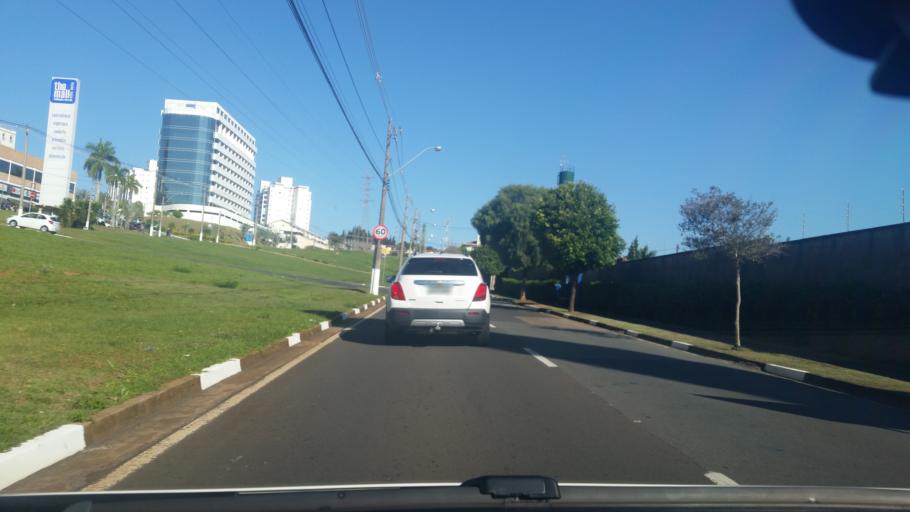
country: BR
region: Sao Paulo
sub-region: Campinas
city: Campinas
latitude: -22.8556
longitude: -47.0571
